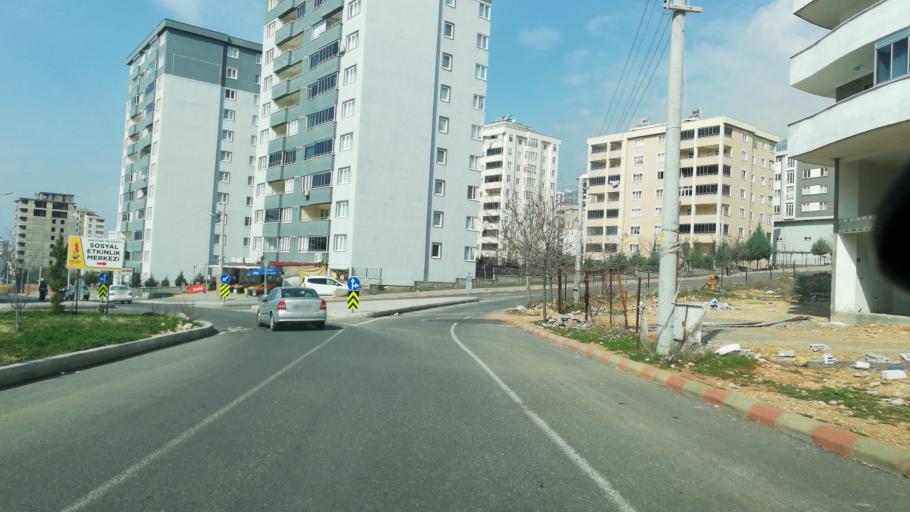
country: TR
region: Kahramanmaras
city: Kahramanmaras
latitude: 37.5865
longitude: 36.8740
